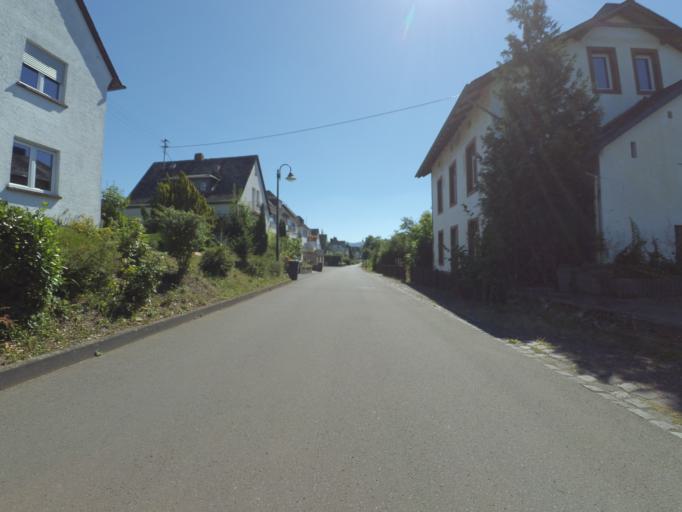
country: DE
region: Rheinland-Pfalz
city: Bullay
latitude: 50.0558
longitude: 7.1351
